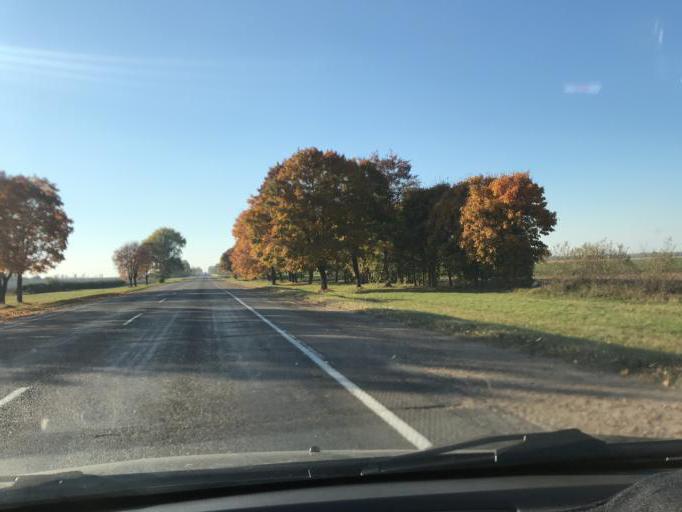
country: BY
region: Minsk
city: Urechcha
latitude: 53.0710
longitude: 27.8085
